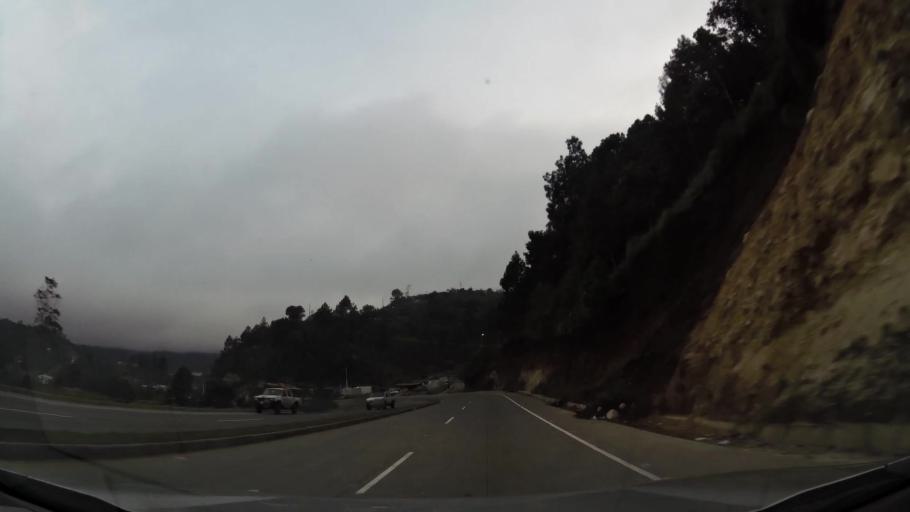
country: GT
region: Solola
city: Concepcion
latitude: 14.8282
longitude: -91.0900
